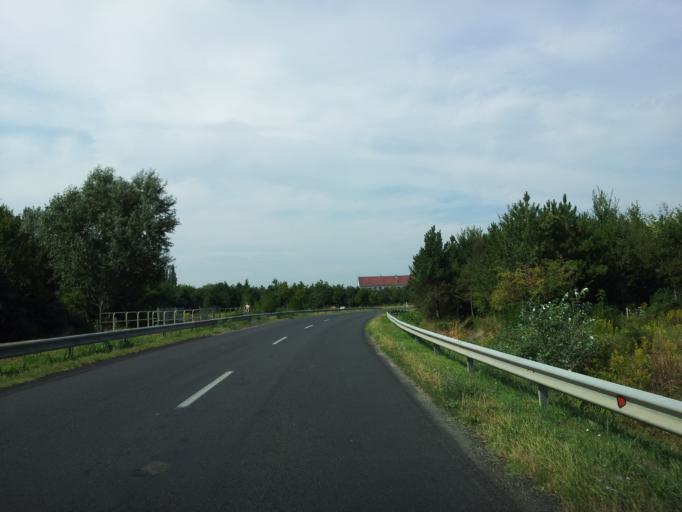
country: HU
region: Veszprem
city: Tapolca
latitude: 46.8837
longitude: 17.4841
